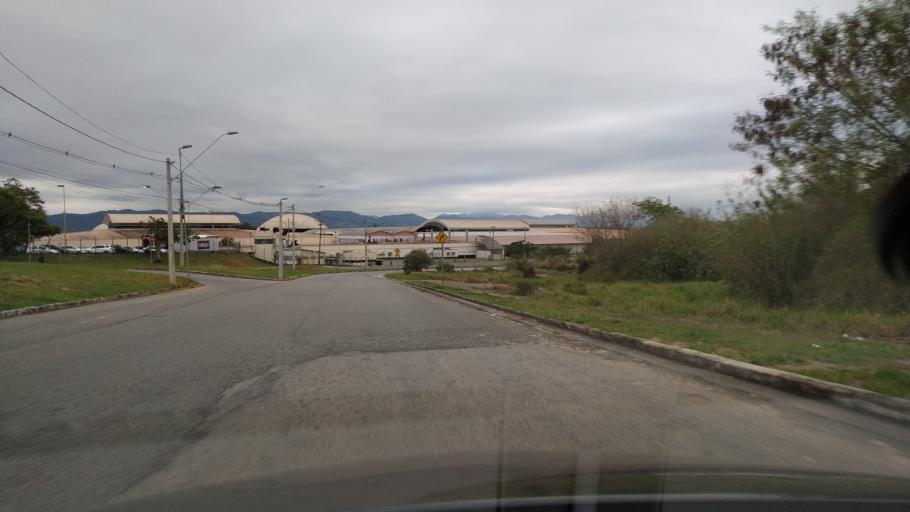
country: BR
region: Sao Paulo
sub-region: Sao Jose Dos Campos
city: Sao Jose dos Campos
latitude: -23.1599
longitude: -45.7914
